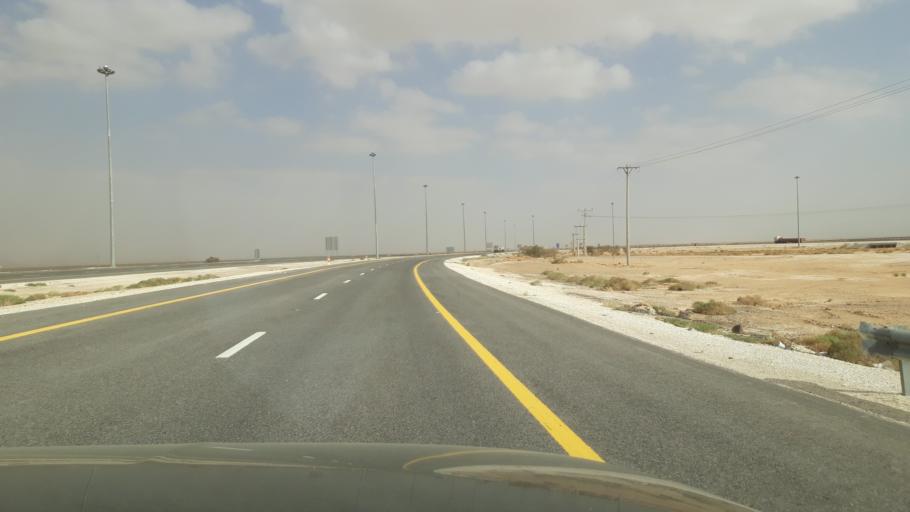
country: JO
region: Amman
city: Al Azraq ash Shamali
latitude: 31.7820
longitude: 36.7919
